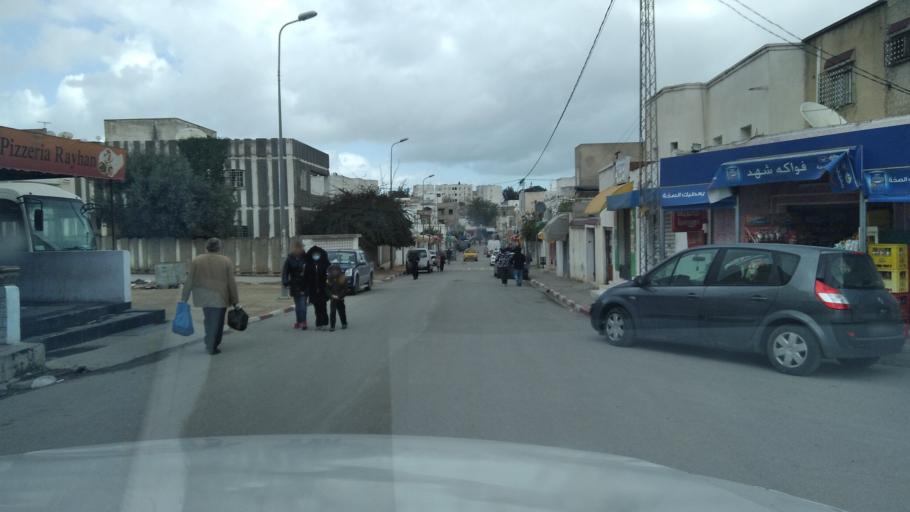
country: TN
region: Bin 'Arus
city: Ben Arous
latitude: 36.7398
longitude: 10.2359
